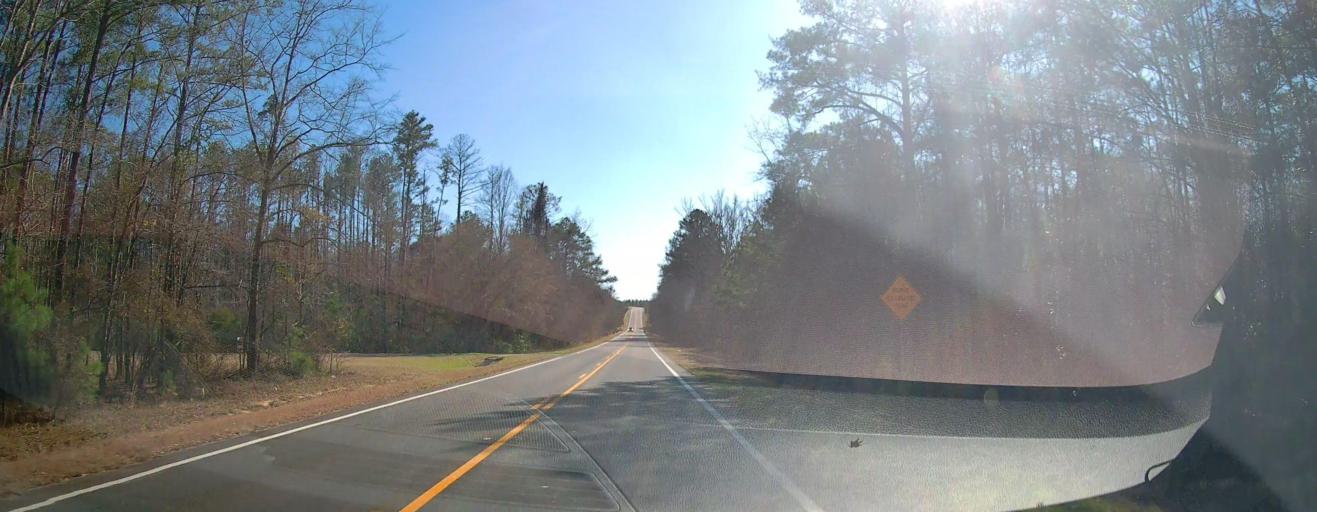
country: US
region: Georgia
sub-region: Macon County
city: Oglethorpe
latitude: 32.2270
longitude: -84.0992
